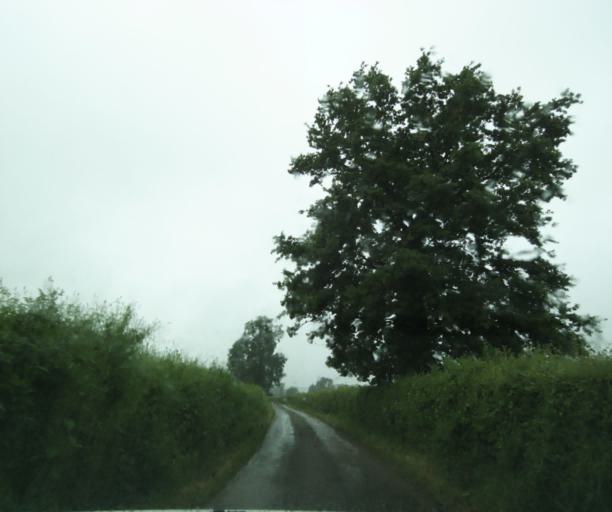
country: FR
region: Bourgogne
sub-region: Departement de Saone-et-Loire
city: Charolles
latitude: 46.3993
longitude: 4.2380
